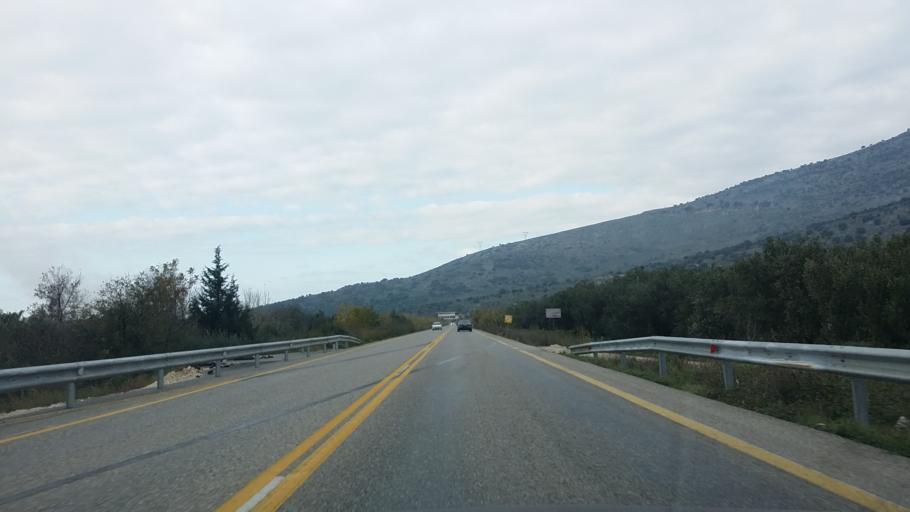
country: GR
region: West Greece
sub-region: Nomos Aitolias kai Akarnanias
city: Mesolongi
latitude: 38.4034
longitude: 21.4040
